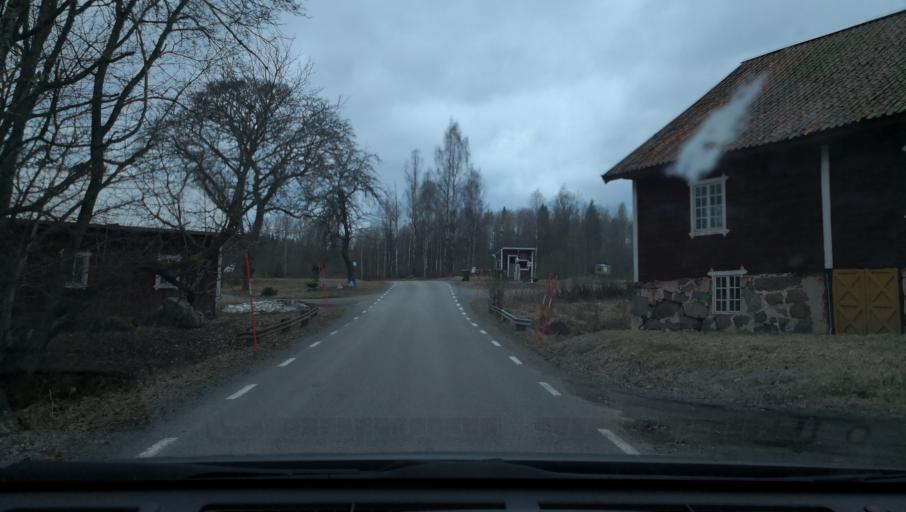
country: SE
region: Vaestmanland
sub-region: Kopings Kommun
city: Kolsva
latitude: 59.5684
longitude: 15.7306
